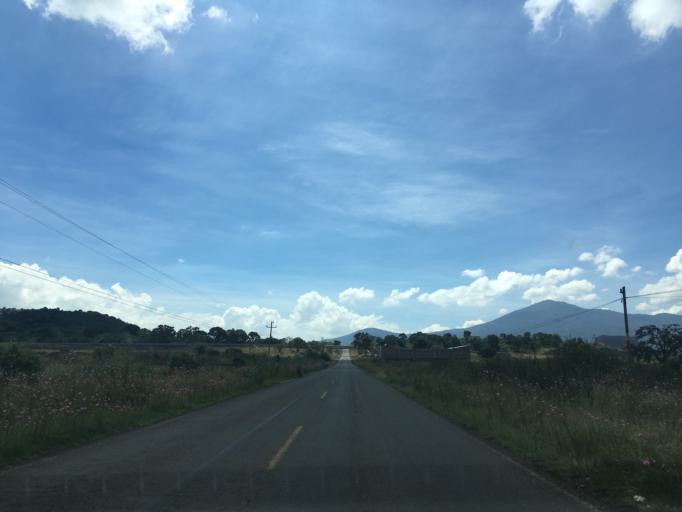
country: MX
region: Michoacan
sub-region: Morelia
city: Cuto de la Esperanza
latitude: 19.7123
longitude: -101.3409
